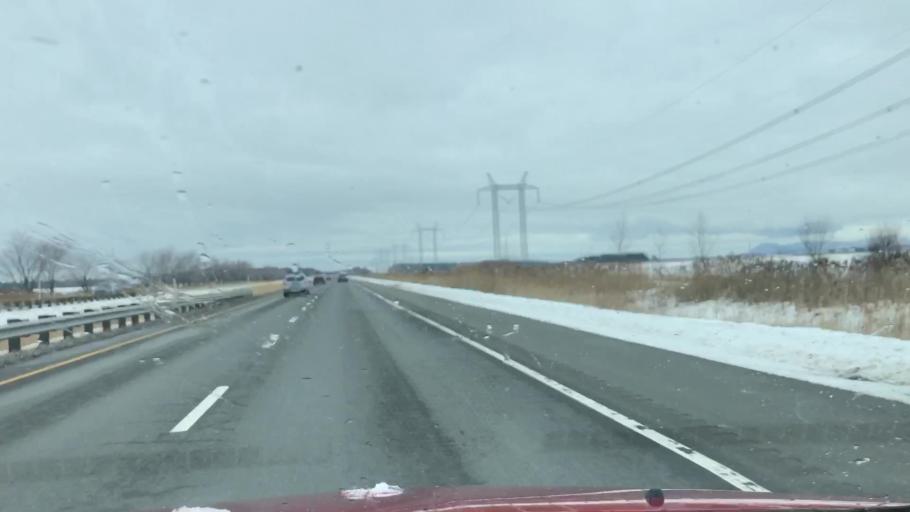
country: CA
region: Quebec
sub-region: Monteregie
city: Rougemont
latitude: 45.3806
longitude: -73.0565
